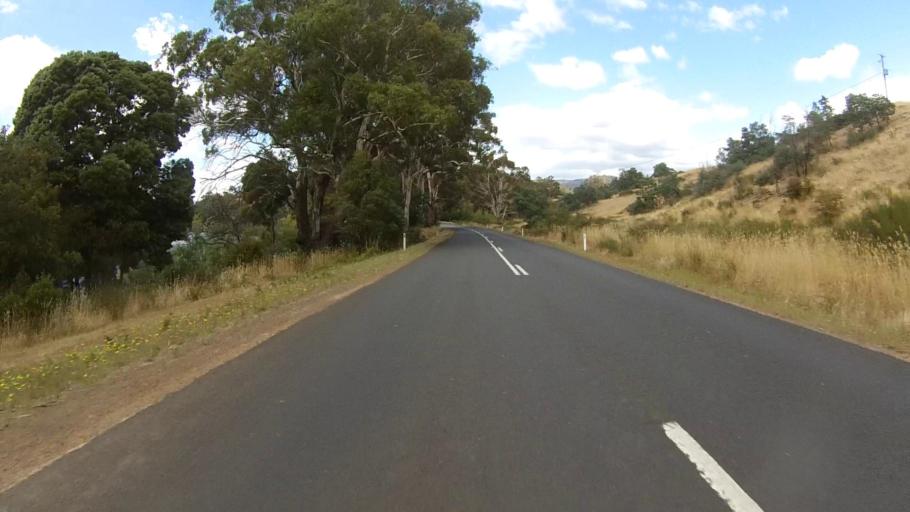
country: AU
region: Tasmania
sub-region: Derwent Valley
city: New Norfolk
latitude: -42.7563
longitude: 146.9858
